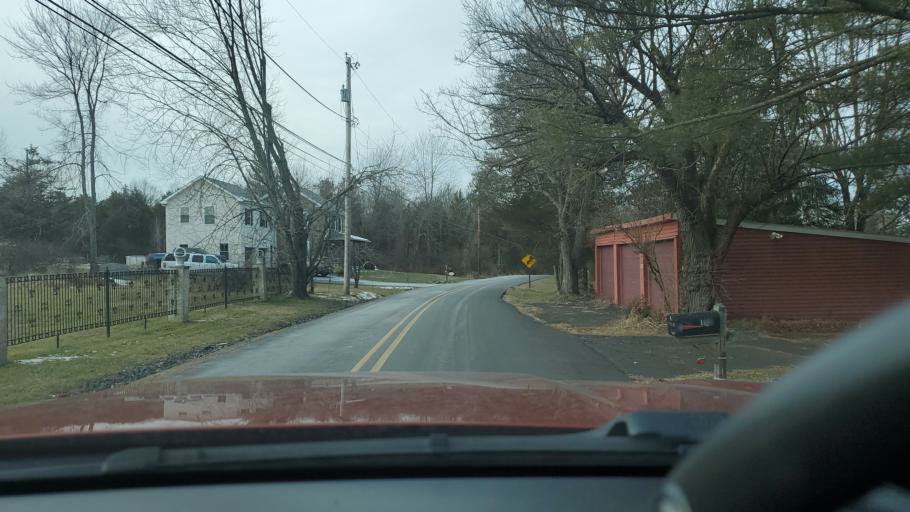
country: US
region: Pennsylvania
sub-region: Montgomery County
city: Woxall
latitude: 40.3148
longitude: -75.4978
